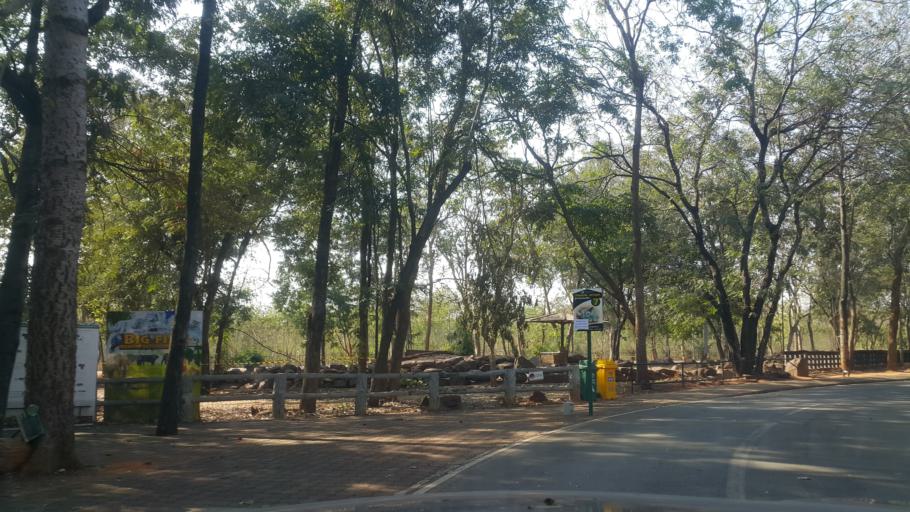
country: TH
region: Nakhon Ratchasima
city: Nakhon Ratchasima
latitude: 14.8552
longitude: 102.0863
